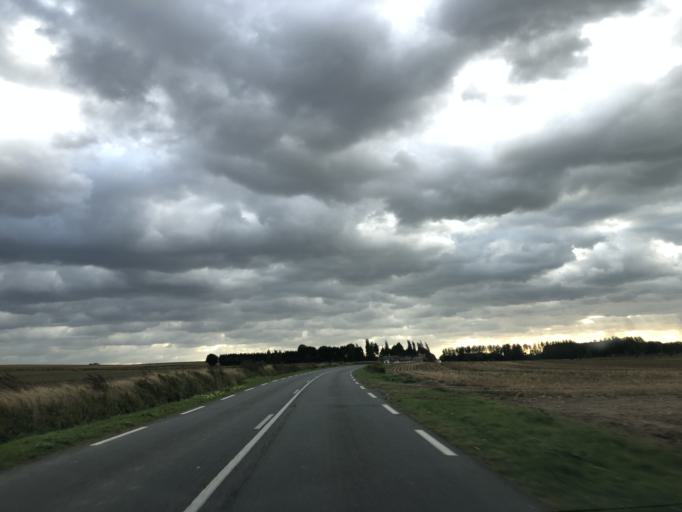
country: FR
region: Picardie
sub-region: Departement de la Somme
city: Cayeux-sur-Mer
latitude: 50.1329
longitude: 1.5074
